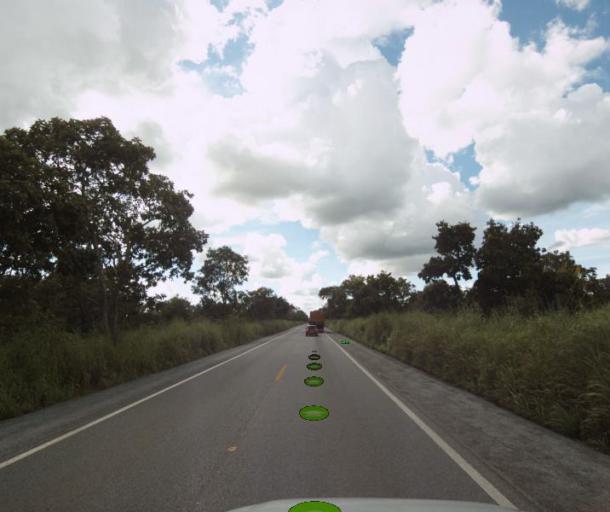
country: BR
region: Goias
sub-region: Porangatu
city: Porangatu
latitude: -13.1850
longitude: -49.1657
